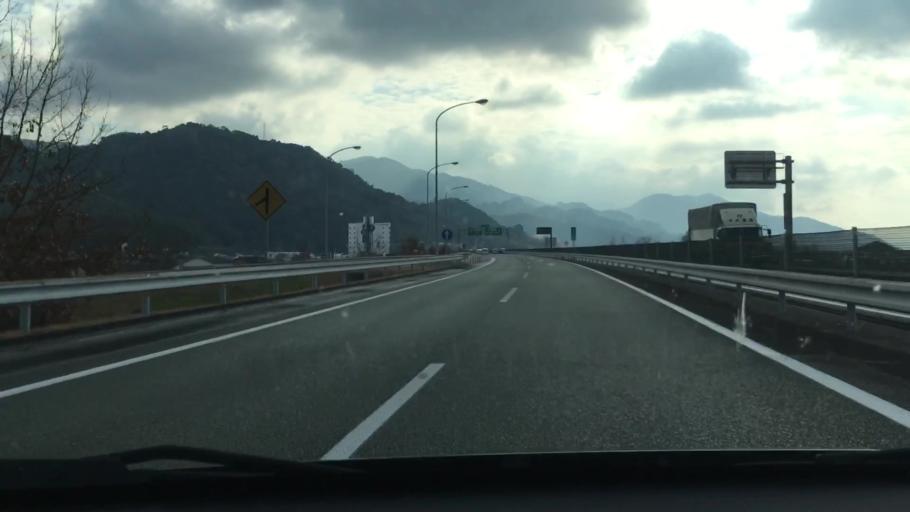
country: JP
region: Kumamoto
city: Yatsushiro
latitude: 32.5123
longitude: 130.6476
